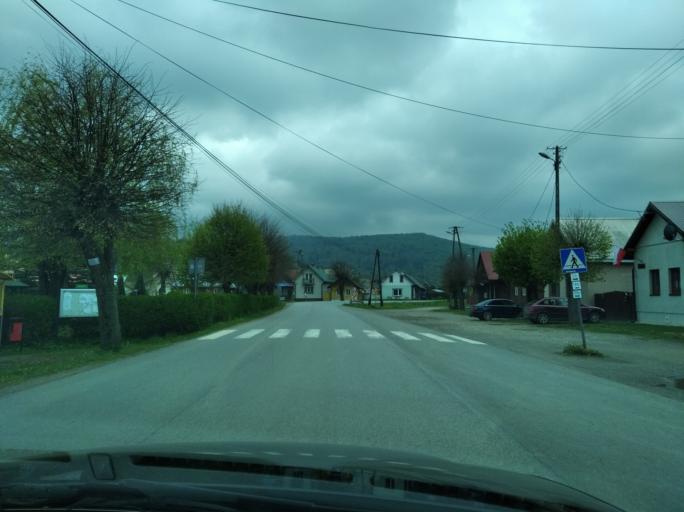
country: PL
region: Subcarpathian Voivodeship
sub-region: Powiat sanocki
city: Sanok
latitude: 49.6193
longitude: 22.2730
